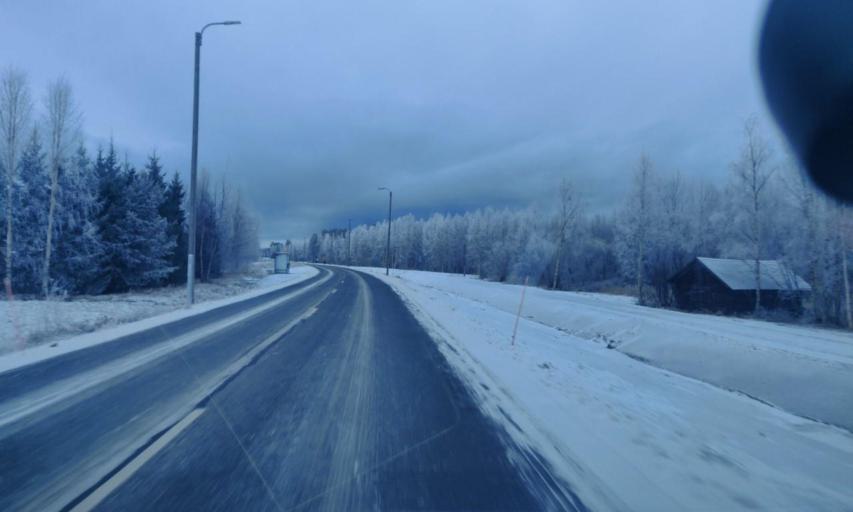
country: FI
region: Northern Ostrobothnia
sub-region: Oulu
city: Oulunsalo
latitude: 64.9818
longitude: 25.2715
